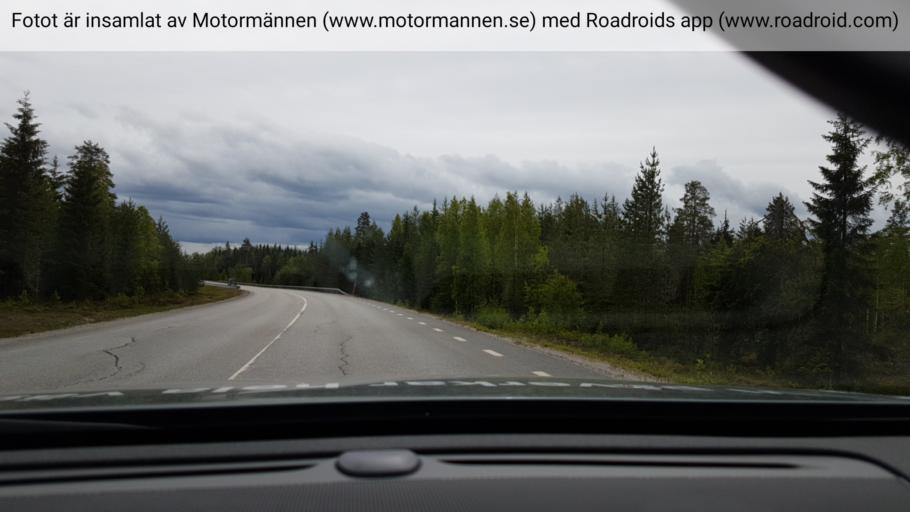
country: SE
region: Vaesterbotten
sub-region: Vannas Kommun
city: Vaennaes
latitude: 64.0125
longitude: 19.6945
